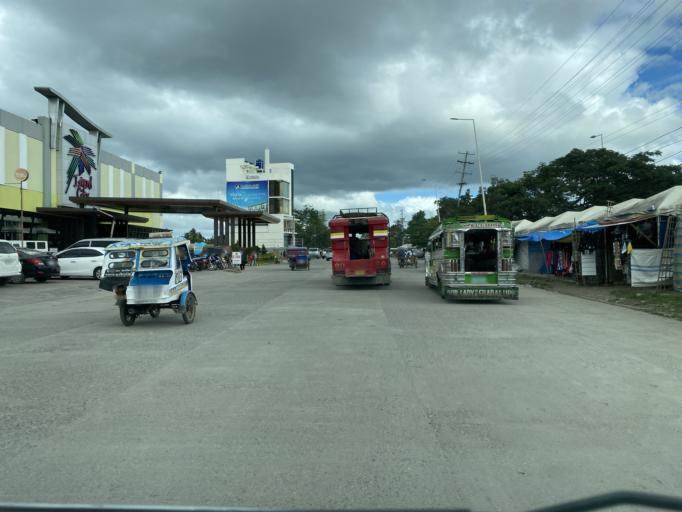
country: PH
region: Central Visayas
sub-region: Province of Bohol
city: Tagbilaran City
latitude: 9.6556
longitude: 123.8704
